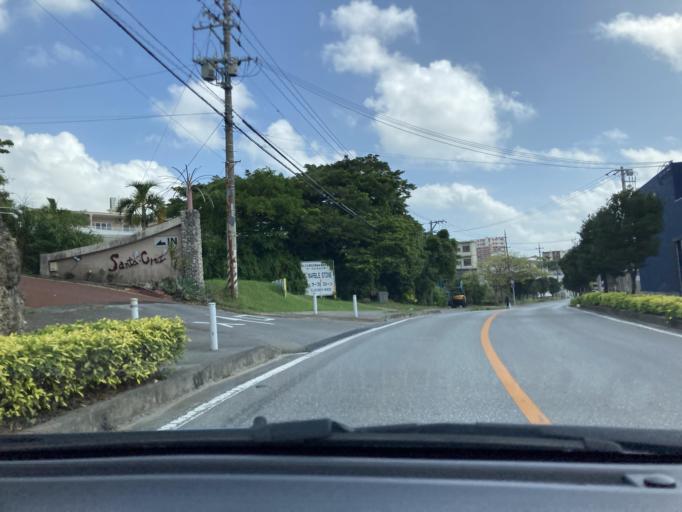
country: JP
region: Okinawa
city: Okinawa
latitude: 26.3213
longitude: 127.8139
